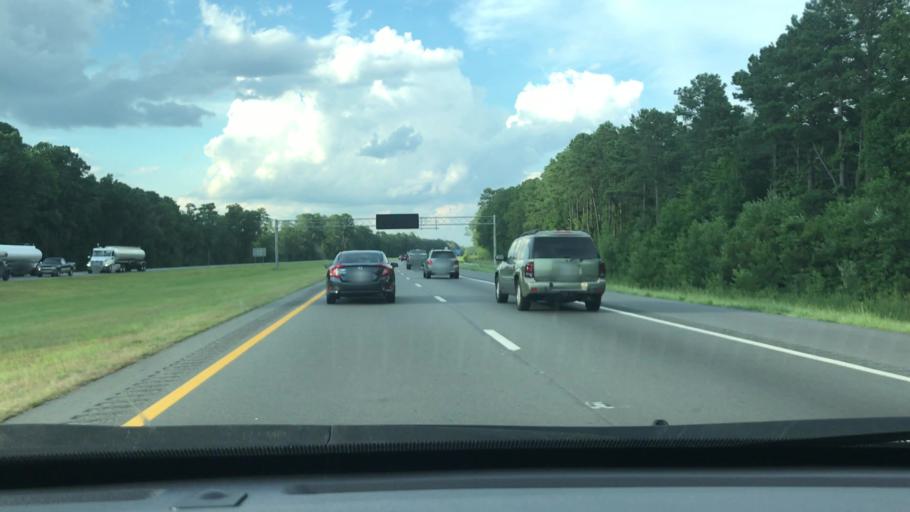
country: US
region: North Carolina
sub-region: Cumberland County
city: Vander
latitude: 35.0112
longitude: -78.8183
